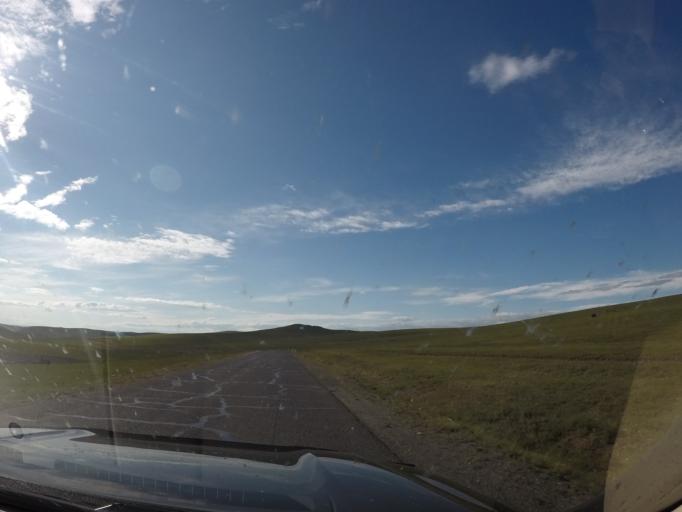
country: MN
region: Hentiy
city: Modot
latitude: 47.8046
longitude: 108.7368
